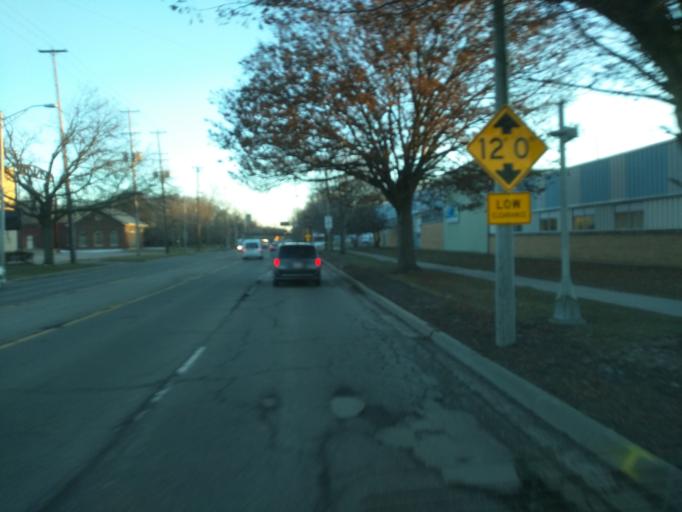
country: US
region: Michigan
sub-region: Ingham County
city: Lansing
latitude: 42.7211
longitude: -84.5382
